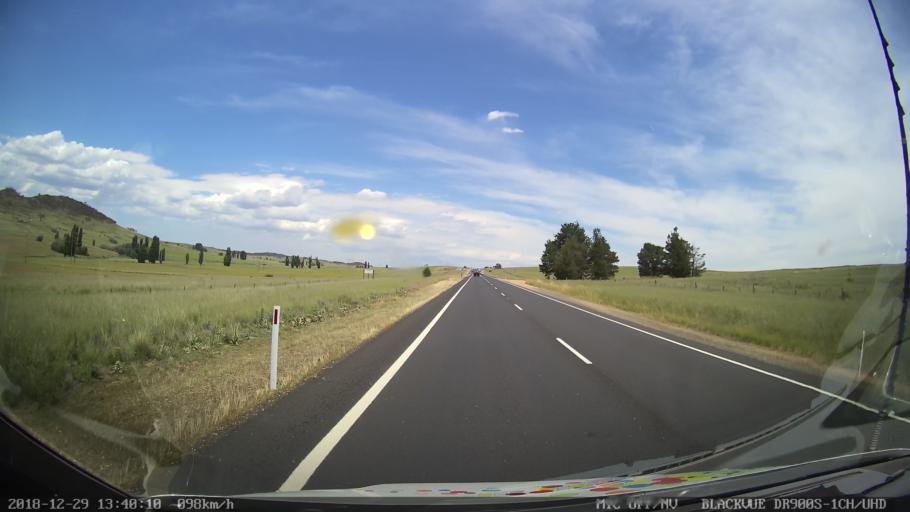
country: AU
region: New South Wales
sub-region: Cooma-Monaro
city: Cooma
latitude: -36.0233
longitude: 149.1507
